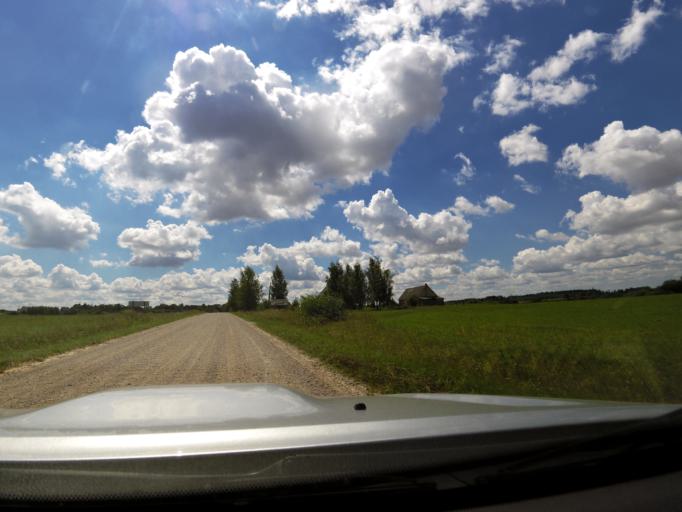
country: LT
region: Vilnius County
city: Elektrenai
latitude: 54.9221
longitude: 24.6571
